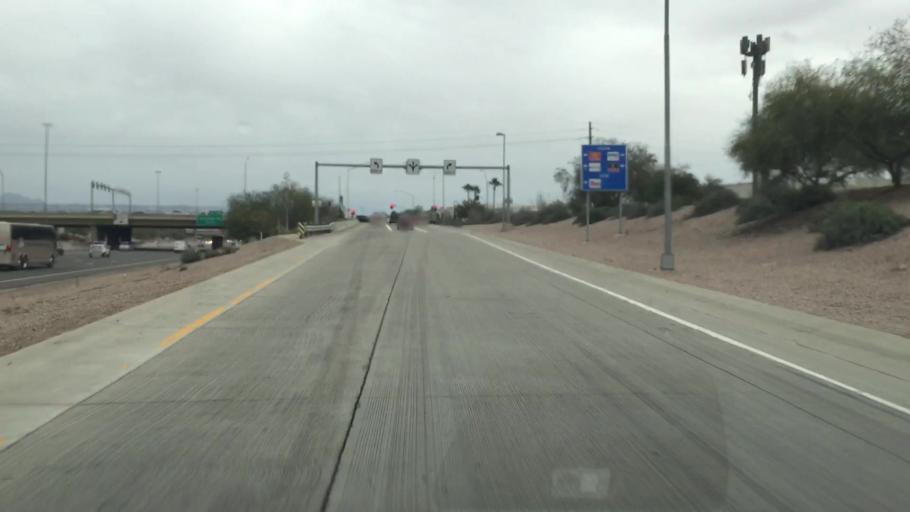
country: US
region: Arizona
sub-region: Maricopa County
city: Gilbert
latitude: 33.3863
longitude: -111.6871
